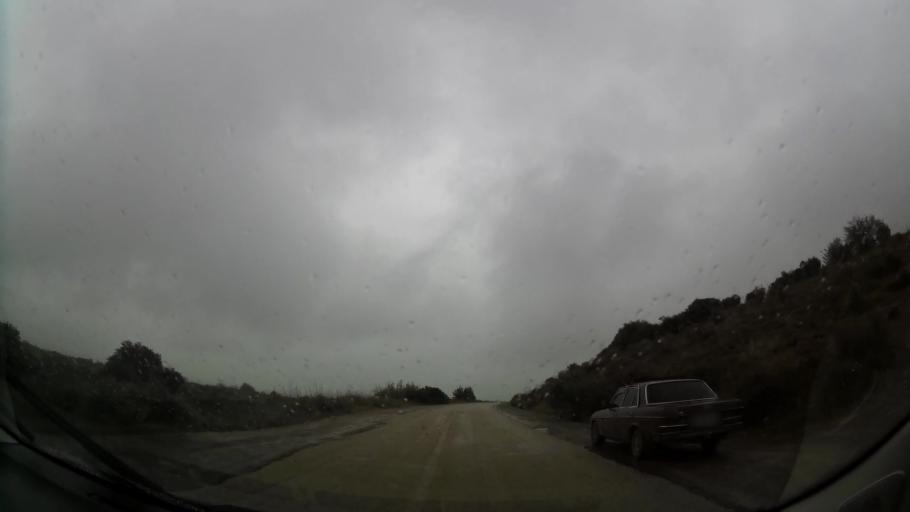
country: MA
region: Taza-Al Hoceima-Taounate
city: Imzourene
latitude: 35.1186
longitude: -3.7795
